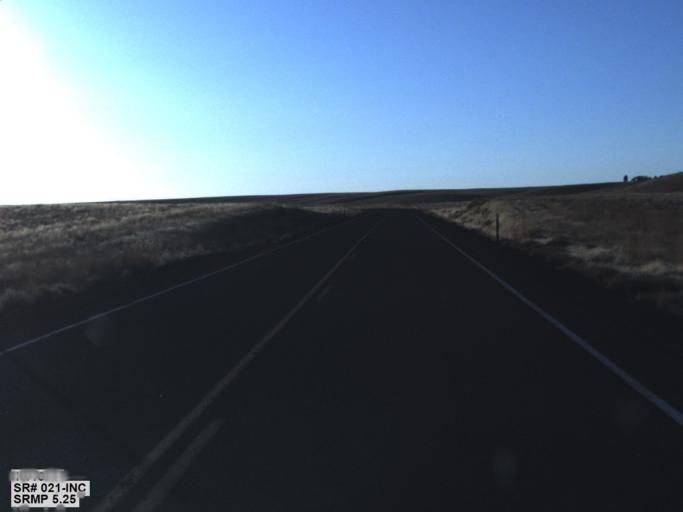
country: US
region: Washington
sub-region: Franklin County
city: Connell
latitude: 46.7105
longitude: -118.5336
